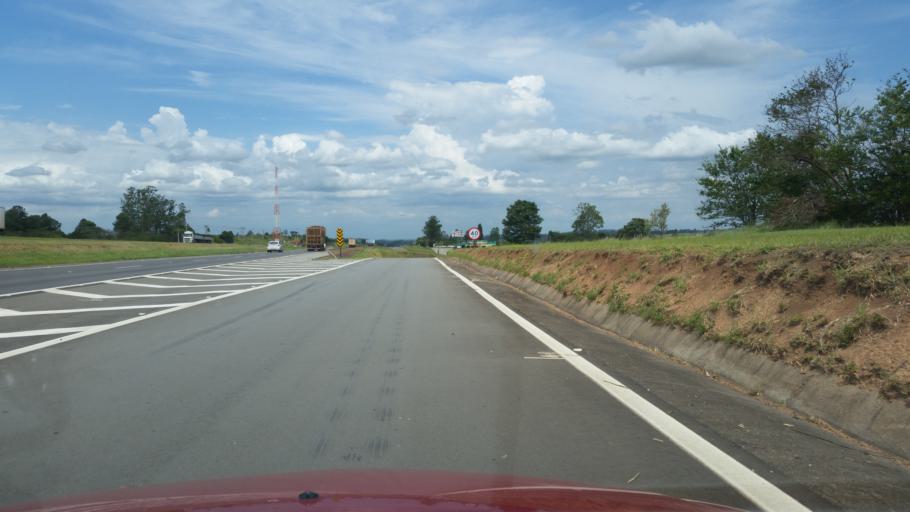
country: BR
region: Sao Paulo
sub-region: Porangaba
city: Porangaba
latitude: -23.2462
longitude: -48.0508
